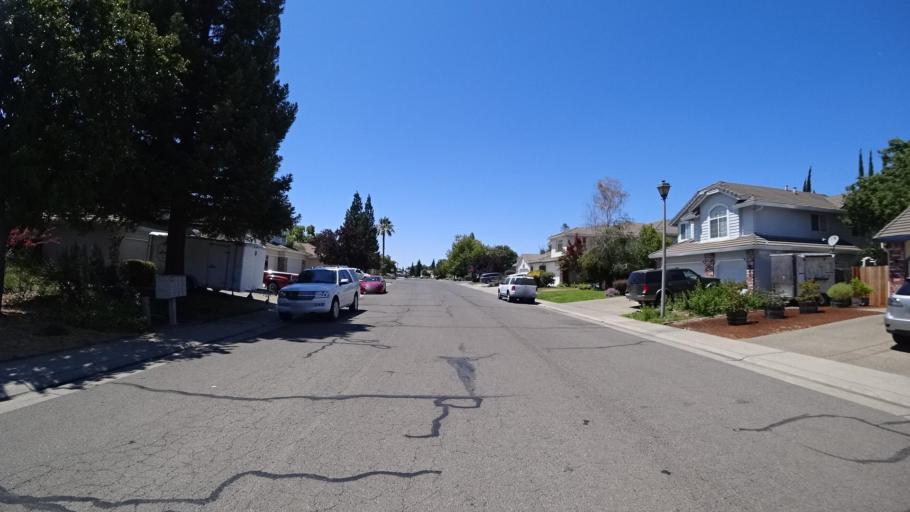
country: US
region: California
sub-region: Placer County
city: Rocklin
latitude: 38.8260
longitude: -121.2576
